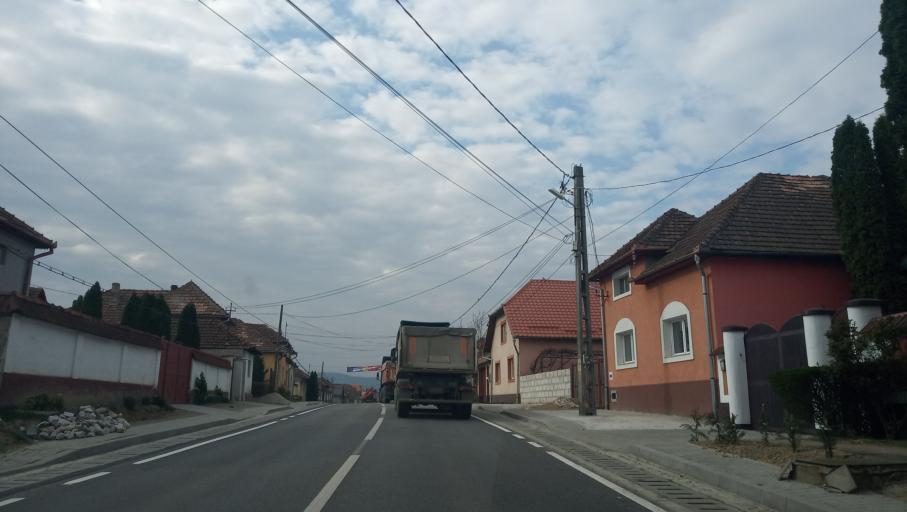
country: RO
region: Bihor
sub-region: Comuna Rieni
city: Rieni
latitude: 46.5596
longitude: 22.4483
